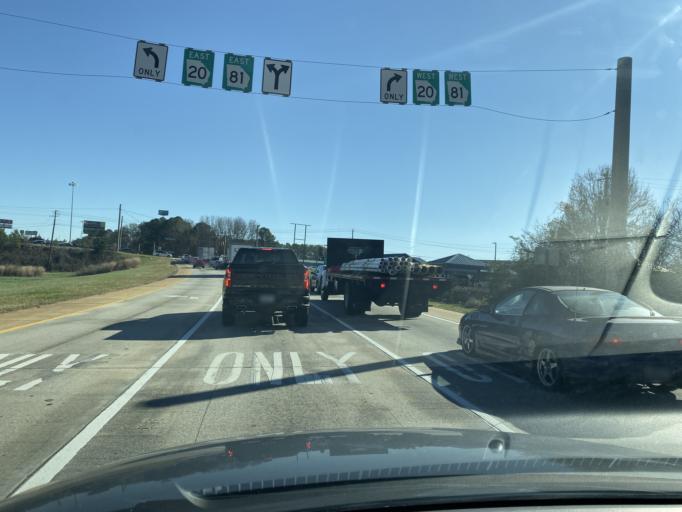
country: US
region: Georgia
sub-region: Henry County
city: McDonough
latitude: 33.4276
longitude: -84.1836
